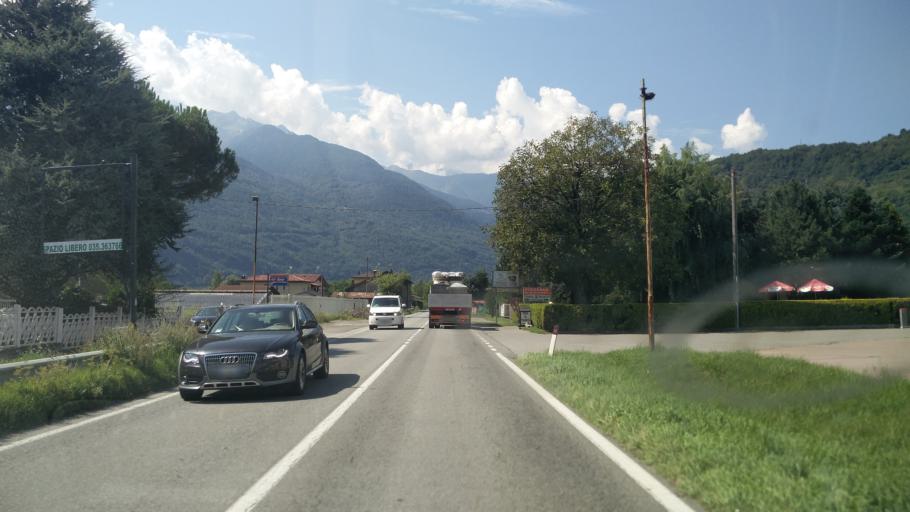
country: IT
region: Lombardy
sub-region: Provincia di Sondrio
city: Bianzone
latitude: 46.1760
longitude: 10.1065
